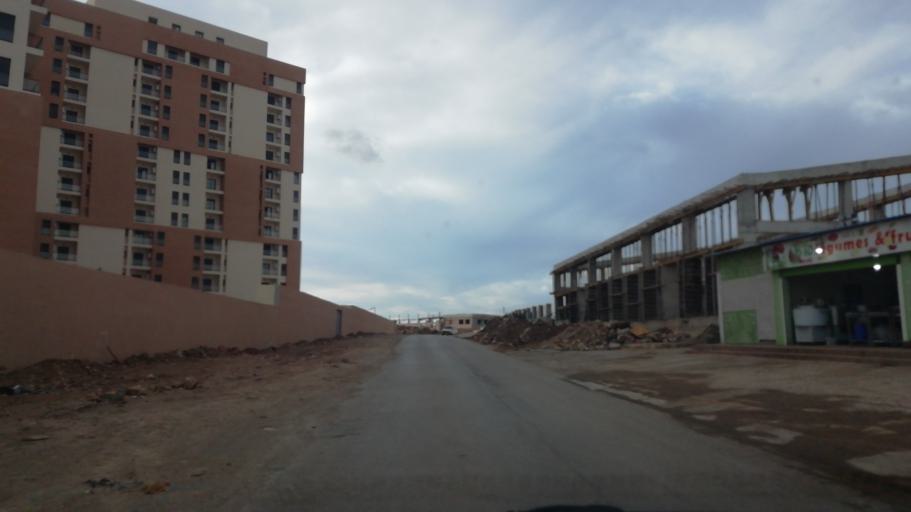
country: DZ
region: Oran
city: Bir el Djir
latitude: 35.7148
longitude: -0.5561
